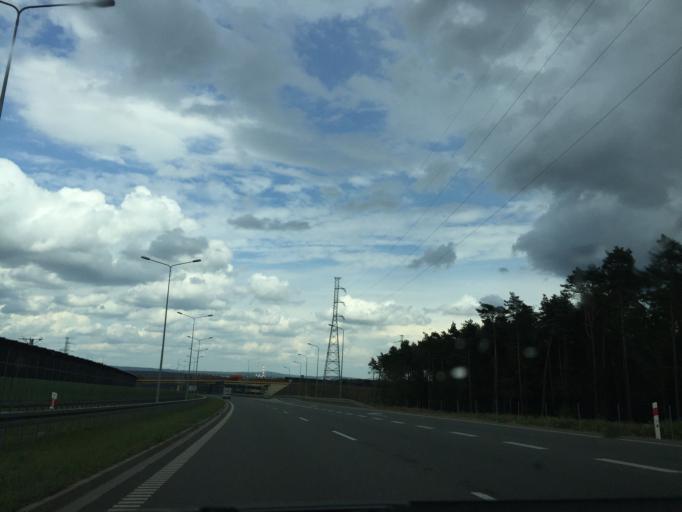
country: PL
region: Swietokrzyskie
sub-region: Powiat kielecki
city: Piekoszow
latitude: 50.8547
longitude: 20.5026
